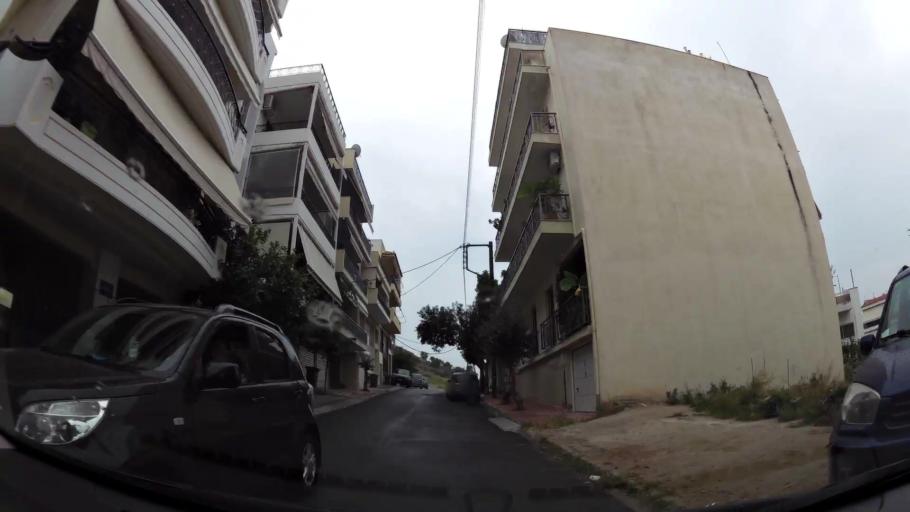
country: GR
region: Attica
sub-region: Nomos Piraios
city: Korydallos
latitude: 37.9953
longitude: 23.6443
